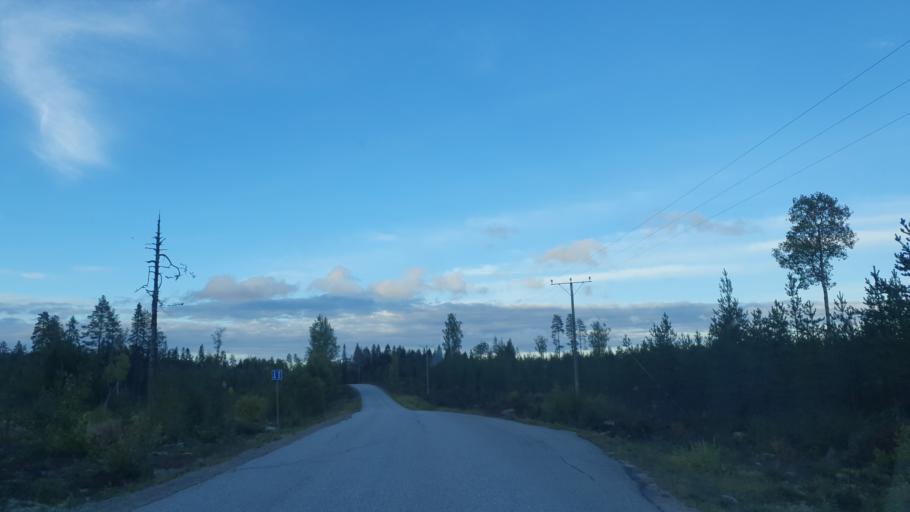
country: FI
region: Kainuu
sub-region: Kehys-Kainuu
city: Kuhmo
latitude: 64.4179
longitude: 29.9613
